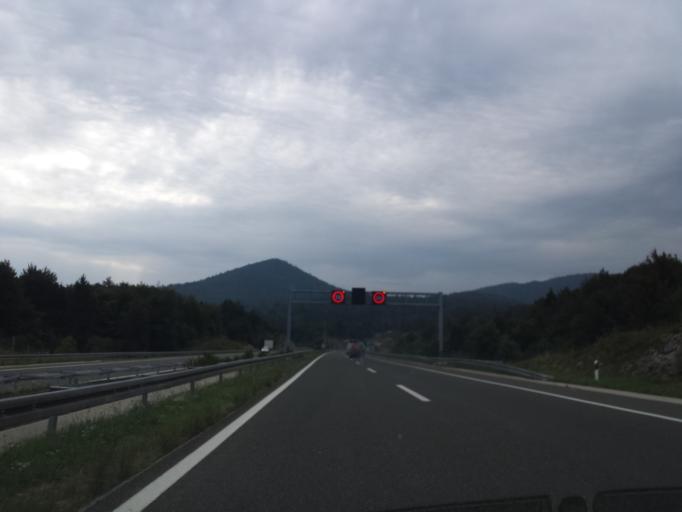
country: HR
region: Karlovacka
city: Ostarije
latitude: 45.1213
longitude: 15.2443
